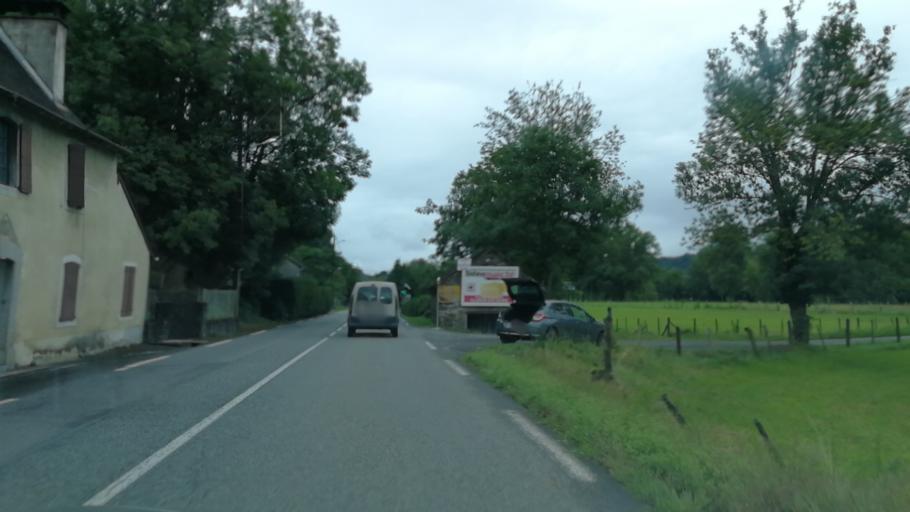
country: FR
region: Aquitaine
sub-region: Departement des Pyrenees-Atlantiques
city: Oloron-Sainte-Marie
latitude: 43.1157
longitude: -0.6162
